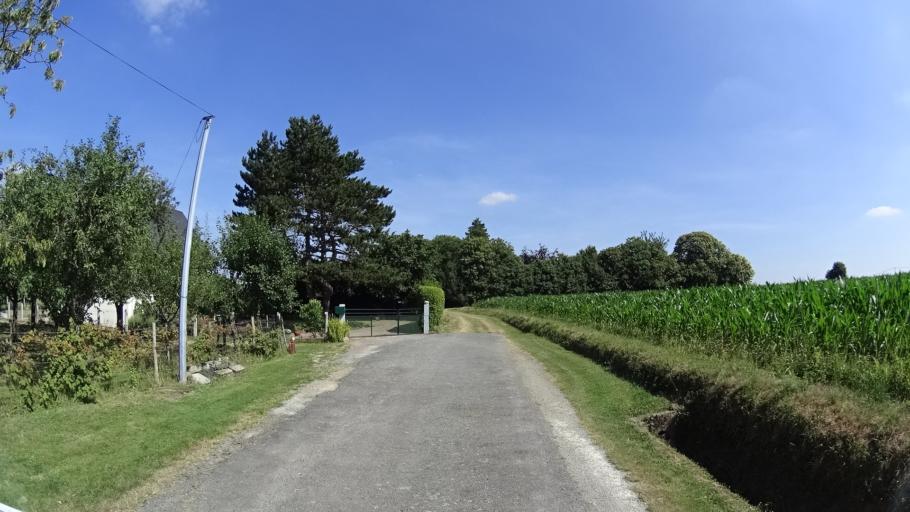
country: FR
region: Brittany
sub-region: Departement d'Ille-et-Vilaine
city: Orgeres
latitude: 47.9870
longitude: -1.6748
